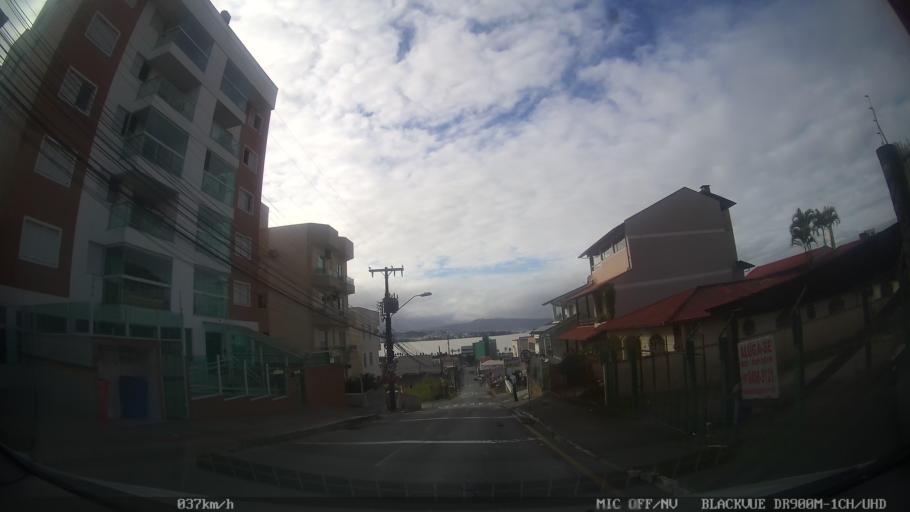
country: BR
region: Santa Catarina
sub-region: Sao Jose
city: Campinas
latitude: -27.6080
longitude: -48.6312
